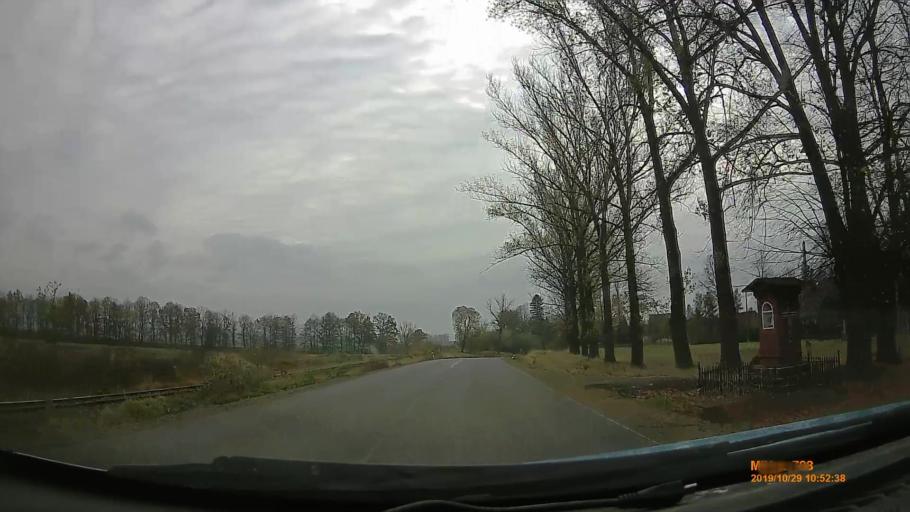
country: PL
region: Lower Silesian Voivodeship
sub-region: Powiat klodzki
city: Nowa Ruda
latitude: 50.5376
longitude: 16.4757
